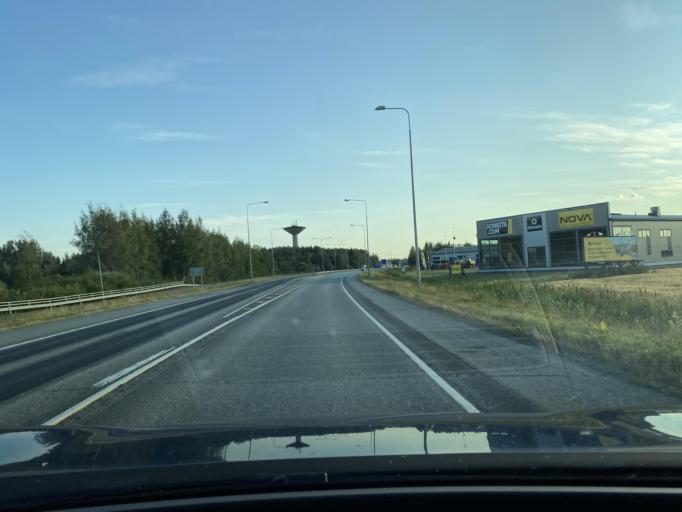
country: FI
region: Southern Ostrobothnia
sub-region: Seinaejoki
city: Nurmo
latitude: 62.8113
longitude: 22.8915
